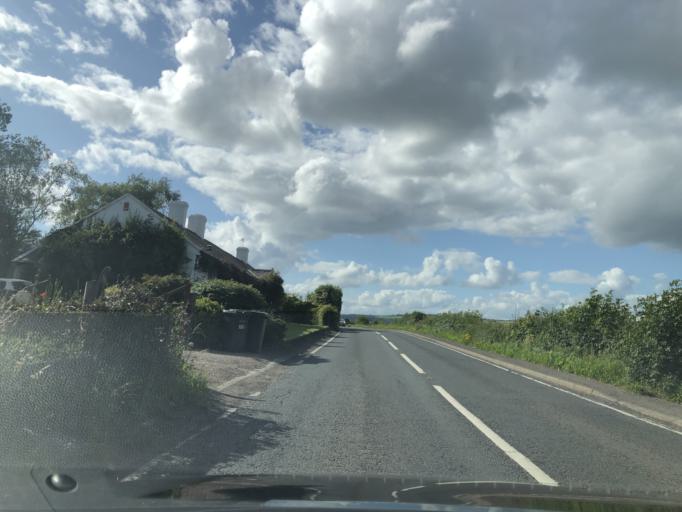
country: GB
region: Northern Ireland
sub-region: Castlereagh District
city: Dundonald
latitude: 54.5725
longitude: -5.7781
